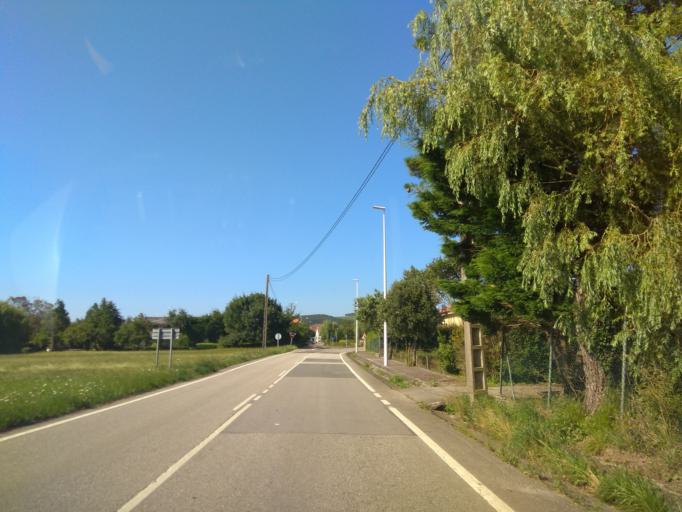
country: ES
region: Cantabria
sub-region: Provincia de Cantabria
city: Bareyo
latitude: 43.4634
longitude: -3.6734
